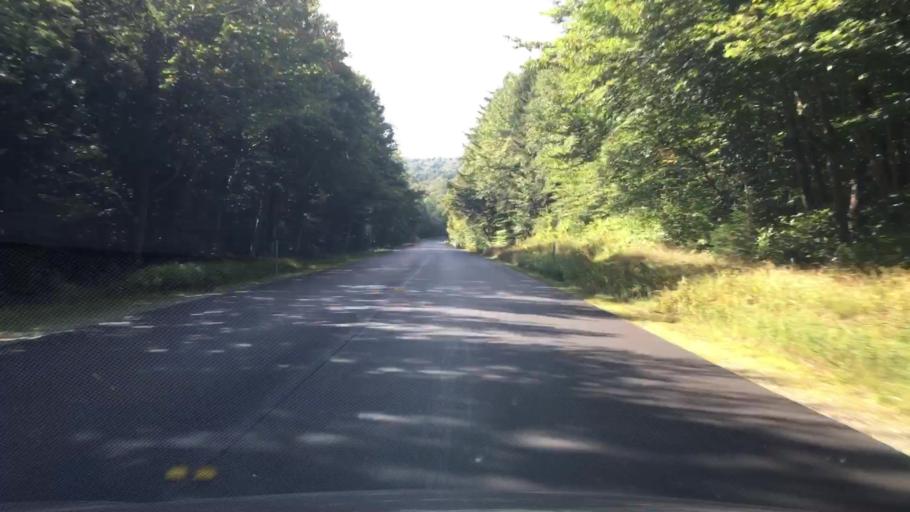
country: US
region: New Hampshire
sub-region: Carroll County
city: Tamworth
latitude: 44.0040
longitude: -71.4185
